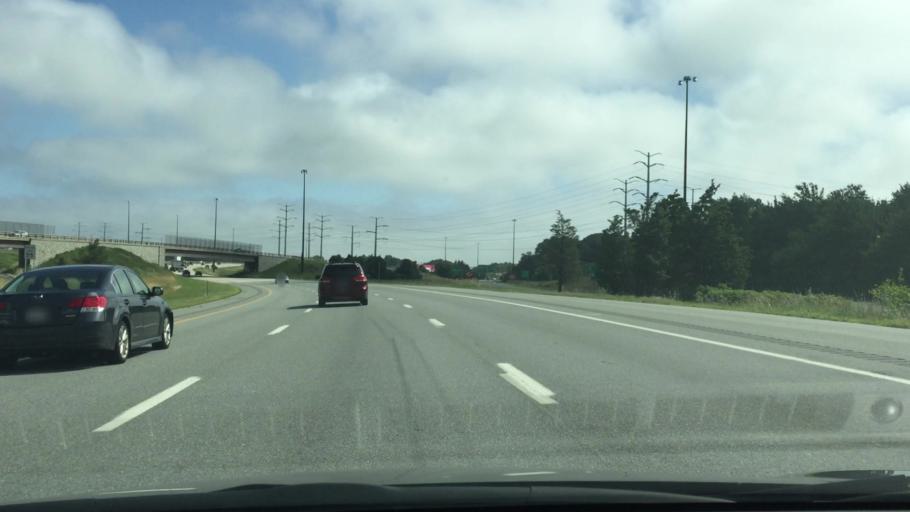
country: US
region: New Hampshire
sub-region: Rockingham County
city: Portsmouth
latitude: 43.0678
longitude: -70.7883
